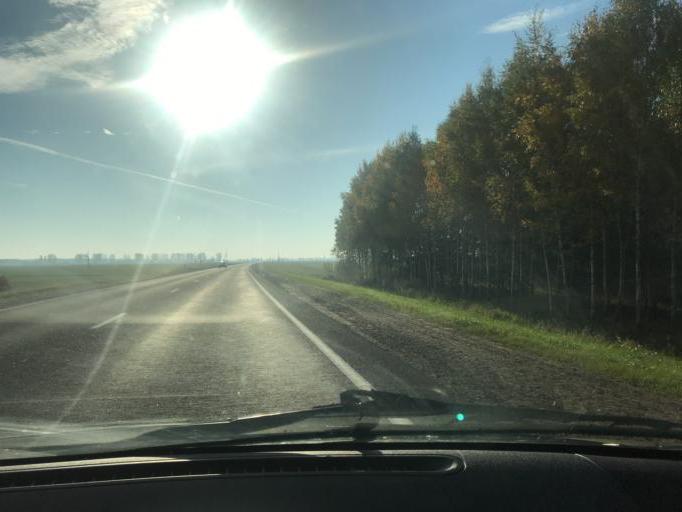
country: BY
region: Brest
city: Drahichyn
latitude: 52.1779
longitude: 25.3074
